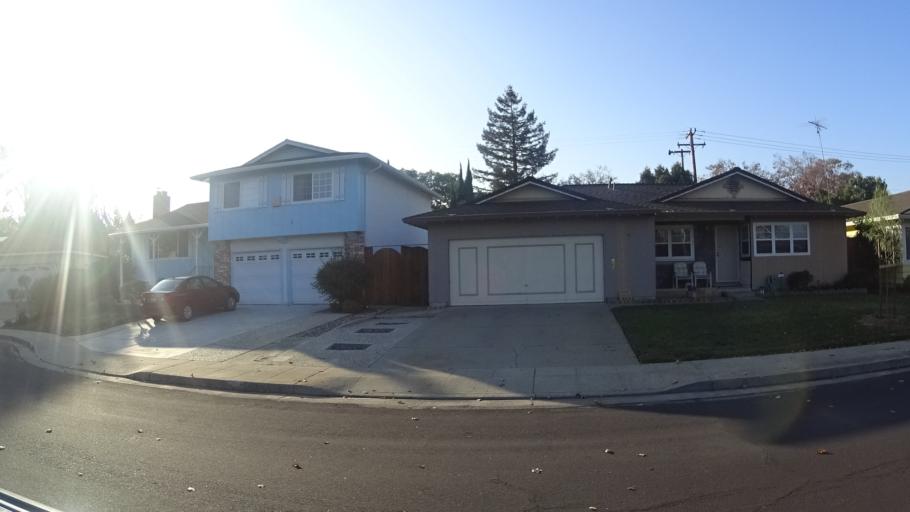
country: US
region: California
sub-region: Santa Clara County
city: Santa Clara
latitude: 37.3429
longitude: -121.9899
